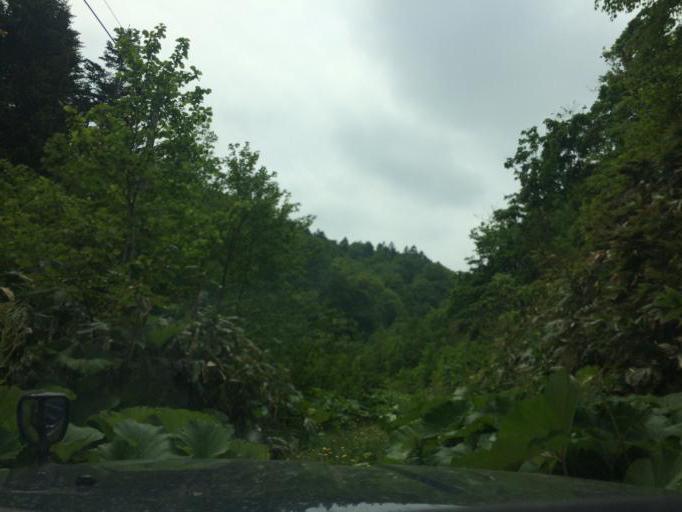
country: JP
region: Hokkaido
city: Niseko Town
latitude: 42.6332
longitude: 140.5670
